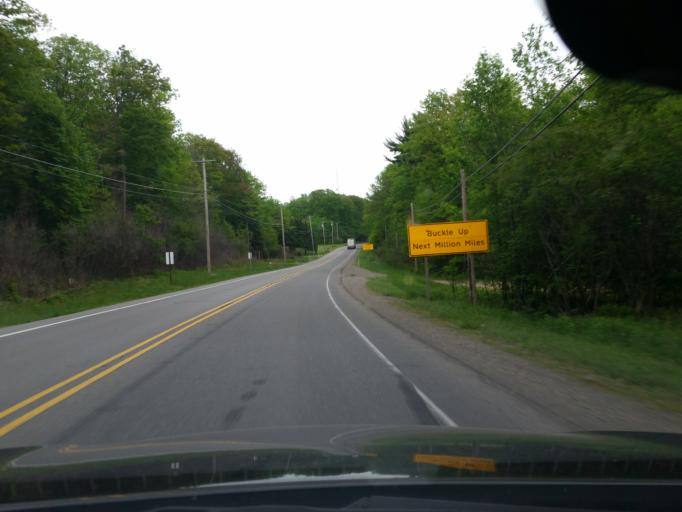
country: US
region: Pennsylvania
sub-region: Elk County
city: Ridgway
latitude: 41.3973
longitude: -78.6970
